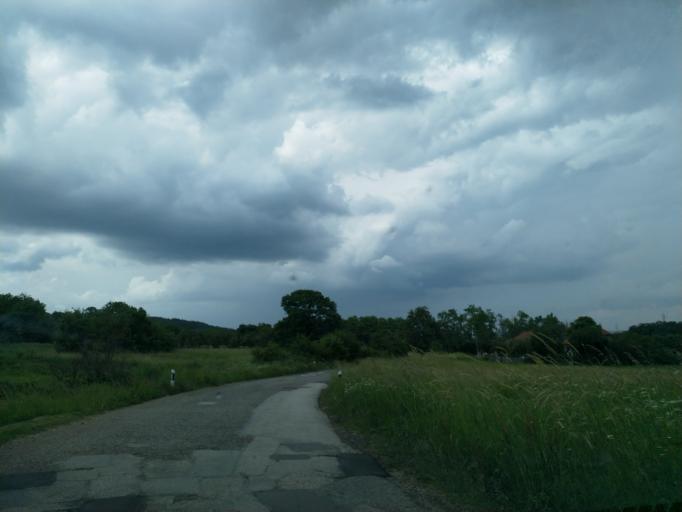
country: RS
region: Central Serbia
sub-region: Zajecarski Okrug
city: Boljevac
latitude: 43.9795
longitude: 21.9725
